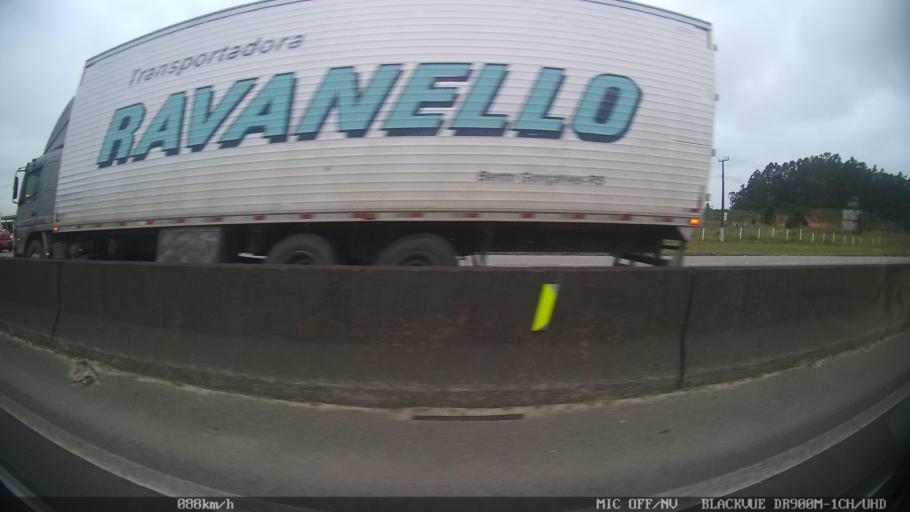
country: BR
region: Santa Catarina
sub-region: Barra Velha
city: Barra Velha
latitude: -26.6306
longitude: -48.7053
